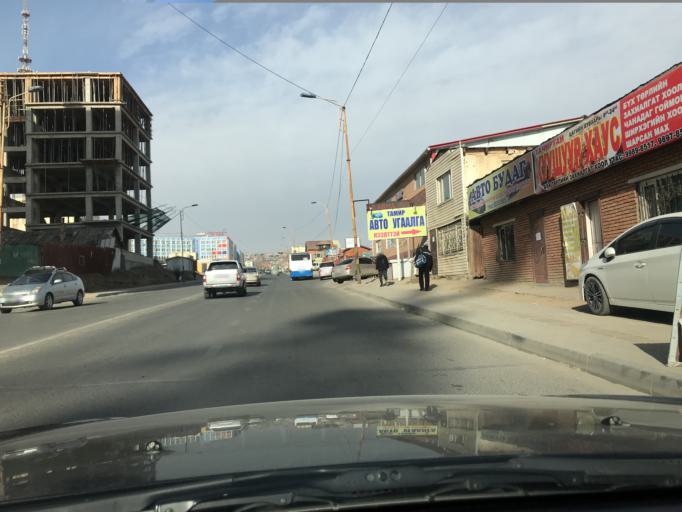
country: MN
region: Ulaanbaatar
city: Ulaanbaatar
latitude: 47.9266
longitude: 106.8940
